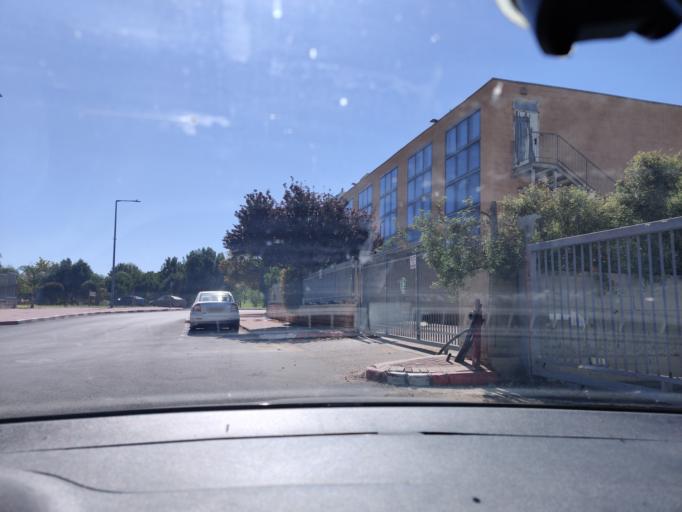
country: IL
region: Southern District
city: Qiryat Gat
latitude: 31.5910
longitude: 34.7845
